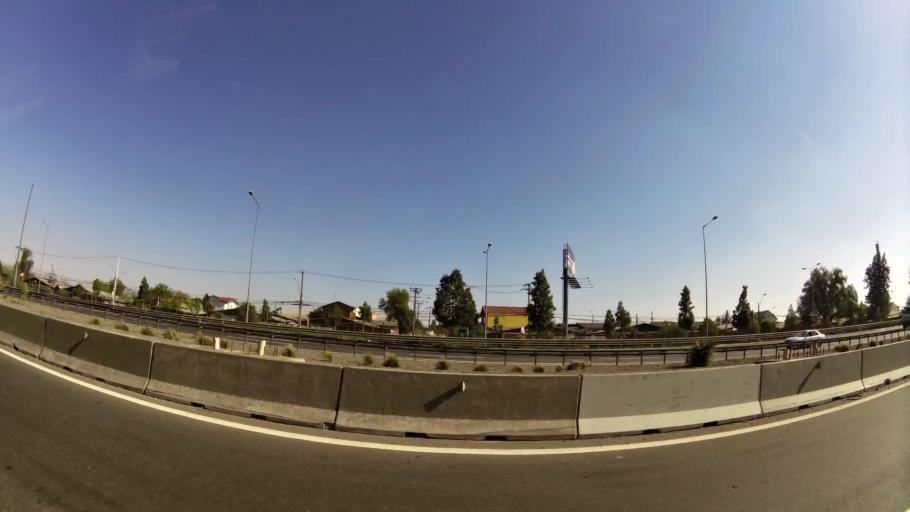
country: CL
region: Santiago Metropolitan
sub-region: Provincia de Santiago
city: Lo Prado
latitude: -33.5025
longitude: -70.7397
